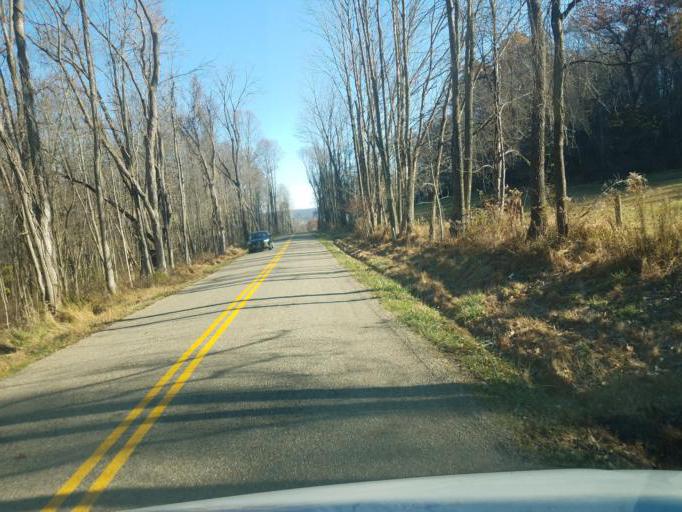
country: US
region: Ohio
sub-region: Richland County
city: Lincoln Heights
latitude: 40.7572
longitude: -82.3948
